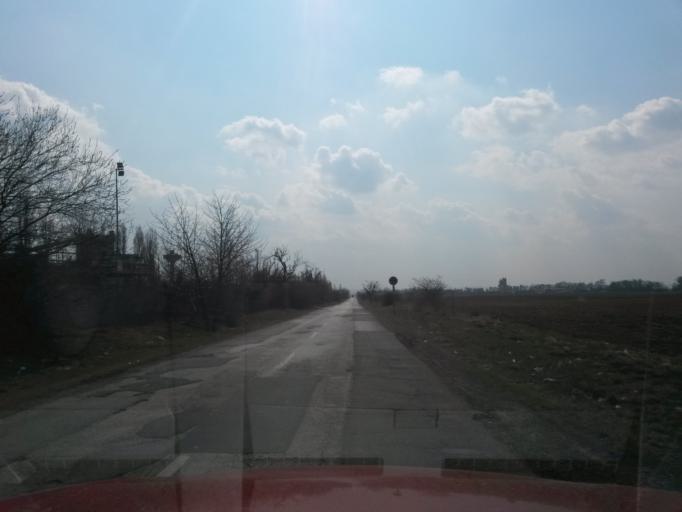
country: SK
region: Kosicky
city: Kosice
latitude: 48.6154
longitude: 21.1787
